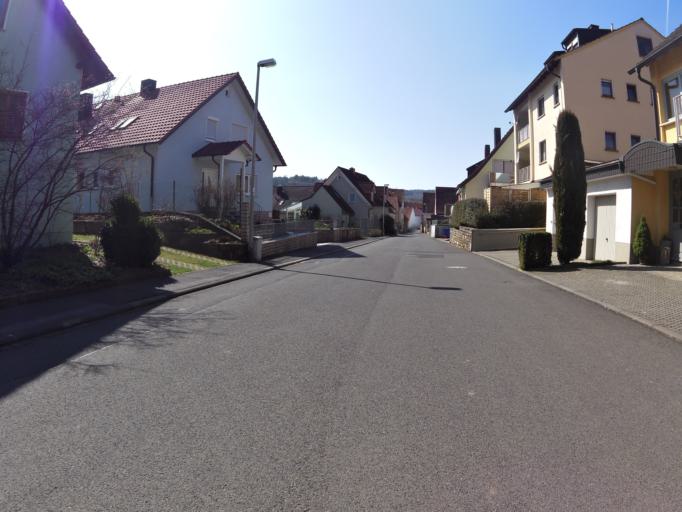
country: DE
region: Bavaria
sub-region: Regierungsbezirk Unterfranken
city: Erlabrunn
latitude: 49.8600
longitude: 9.8137
